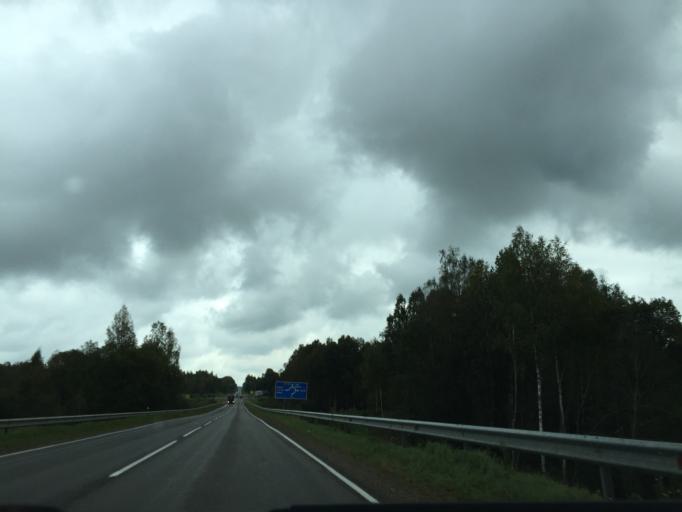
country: LV
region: Rezekne
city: Rezekne
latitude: 56.5458
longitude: 27.3473
